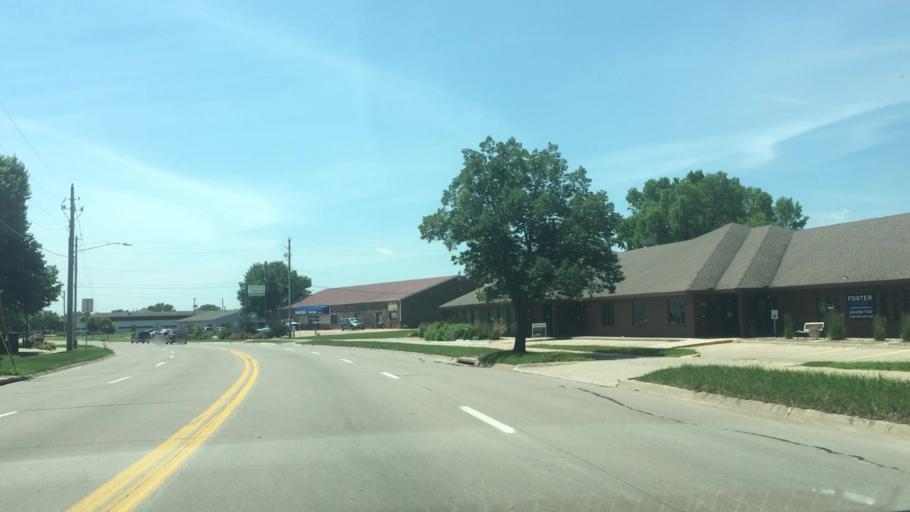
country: US
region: Iowa
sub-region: Johnson County
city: Iowa City
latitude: 41.6443
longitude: -91.5331
